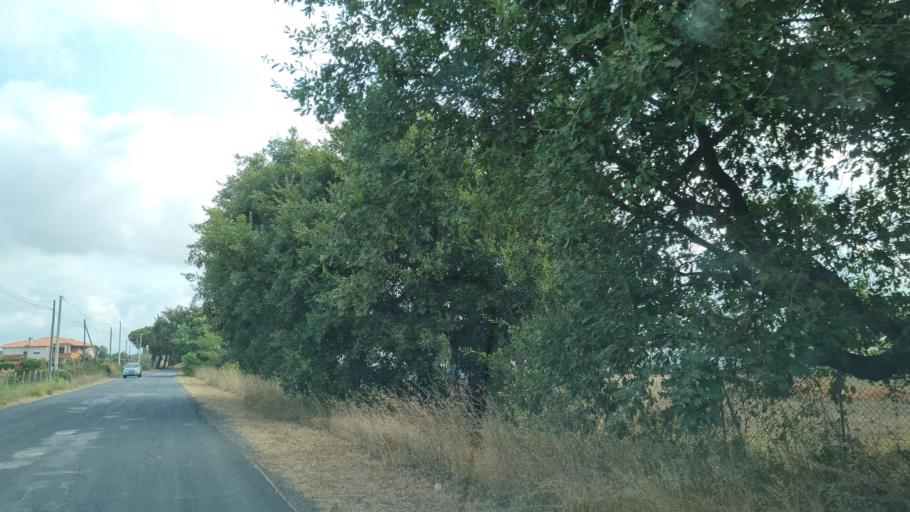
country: IT
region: Latium
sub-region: Provincia di Viterbo
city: Montalto di Castro
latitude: 42.3191
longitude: 11.6111
